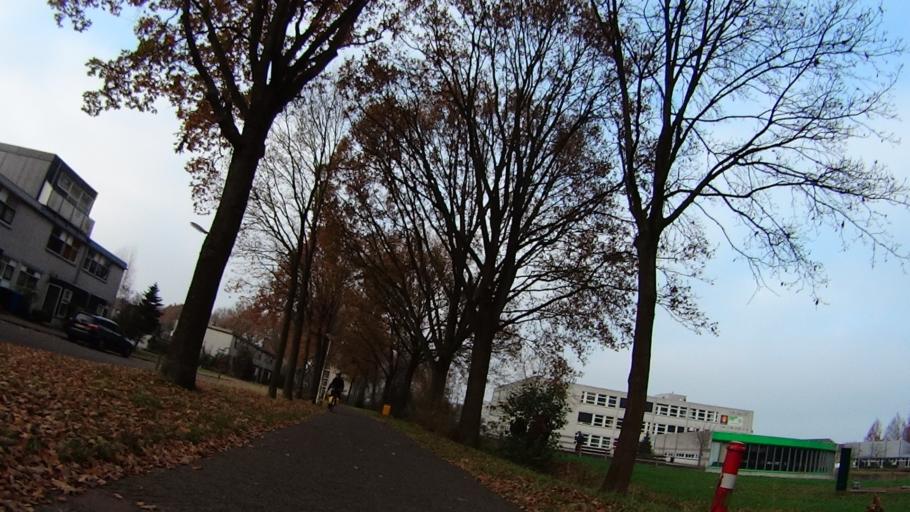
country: NL
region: Utrecht
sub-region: Gemeente Amersfoort
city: Amersfoort
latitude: 52.1773
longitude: 5.4032
